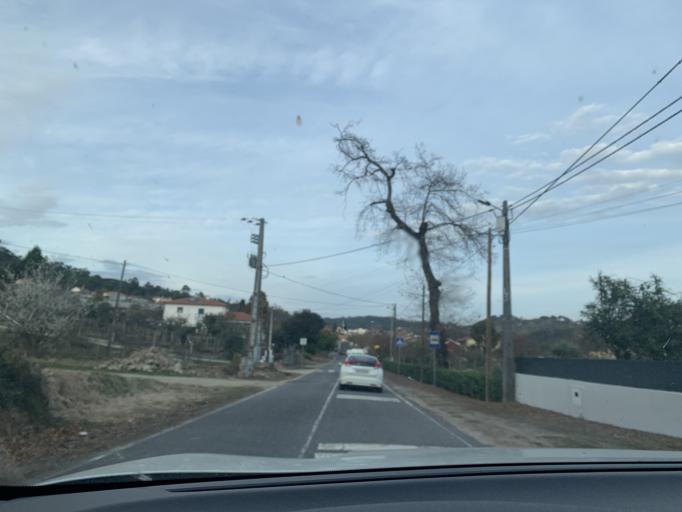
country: PT
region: Viseu
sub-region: Viseu
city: Viseu
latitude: 40.6026
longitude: -7.9850
